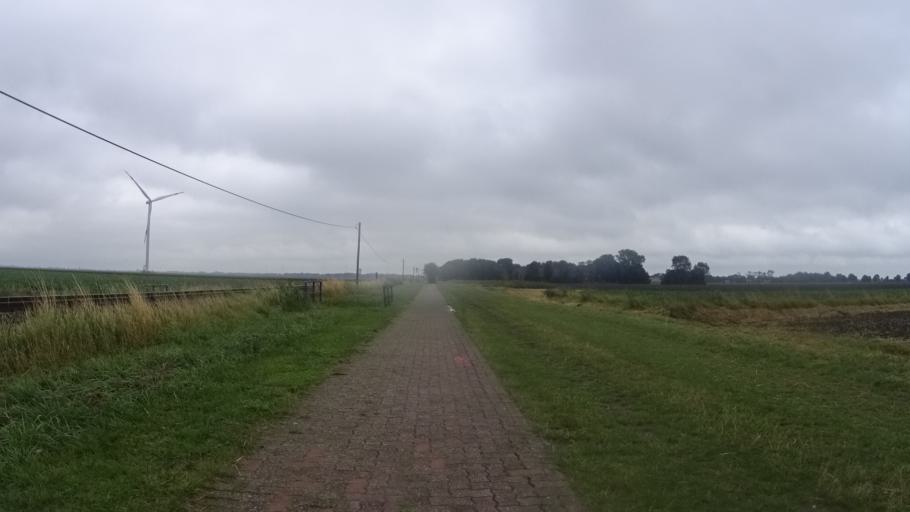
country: DE
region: Lower Saxony
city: Bunde
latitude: 53.1889
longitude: 7.2310
